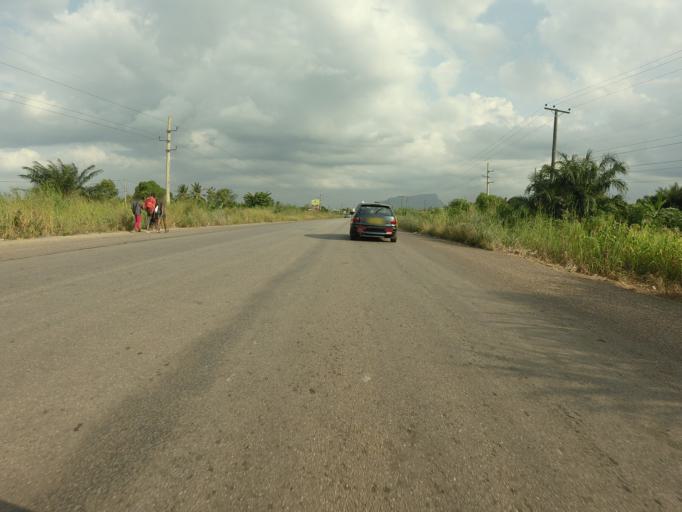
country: GH
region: Volta
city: Ho
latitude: 6.5869
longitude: 0.4793
